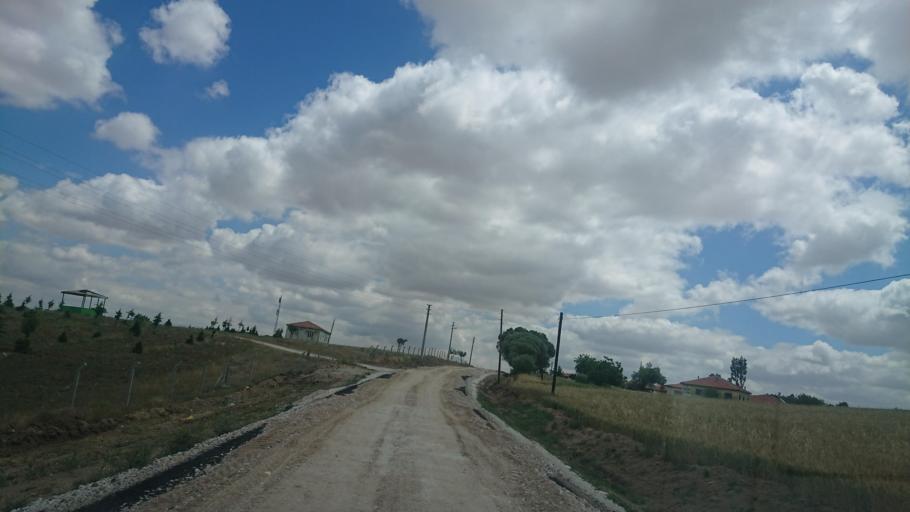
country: TR
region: Aksaray
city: Agacoren
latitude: 38.8628
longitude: 33.9503
